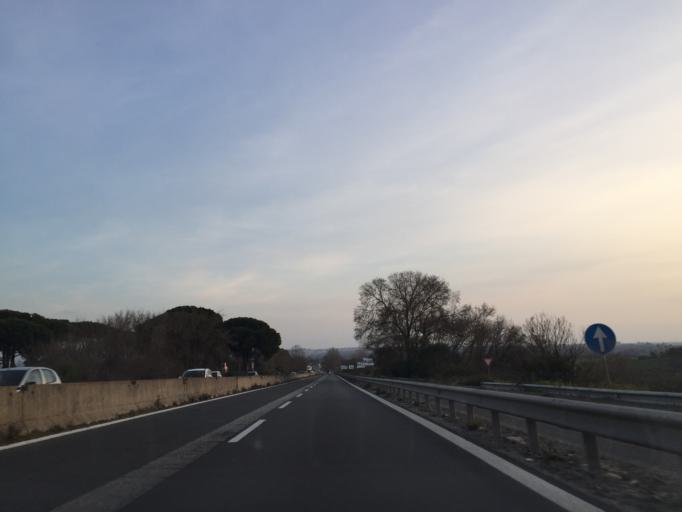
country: IT
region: Latium
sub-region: Citta metropolitana di Roma Capitale
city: Le Rughe
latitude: 42.0704
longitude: 12.3725
